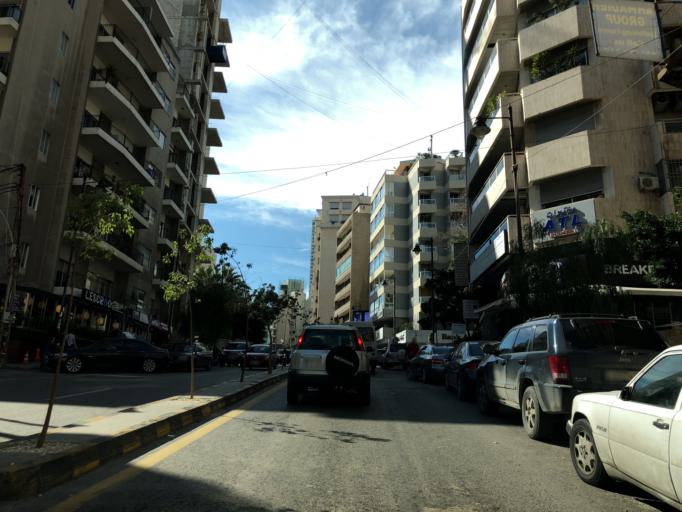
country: LB
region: Beyrouth
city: Beirut
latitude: 33.8879
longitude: 35.5239
